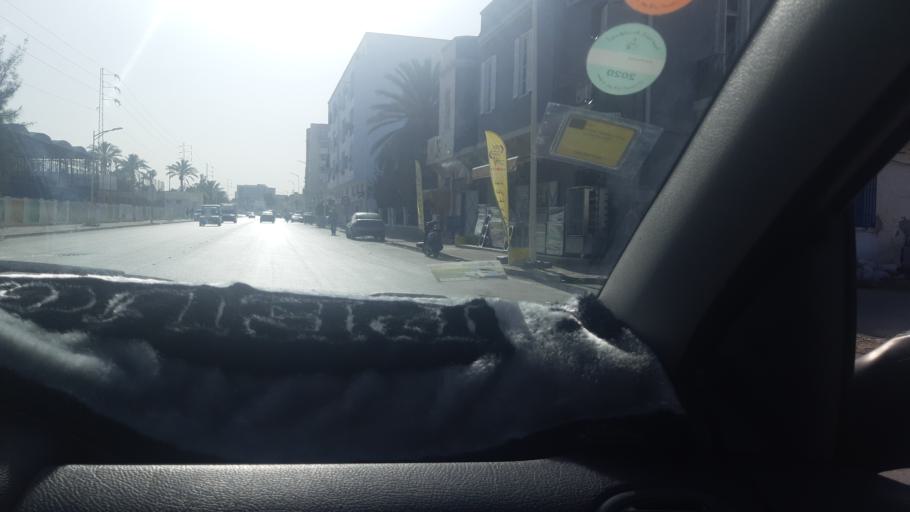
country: TN
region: Safaqis
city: Sfax
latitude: 34.7355
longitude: 10.7473
